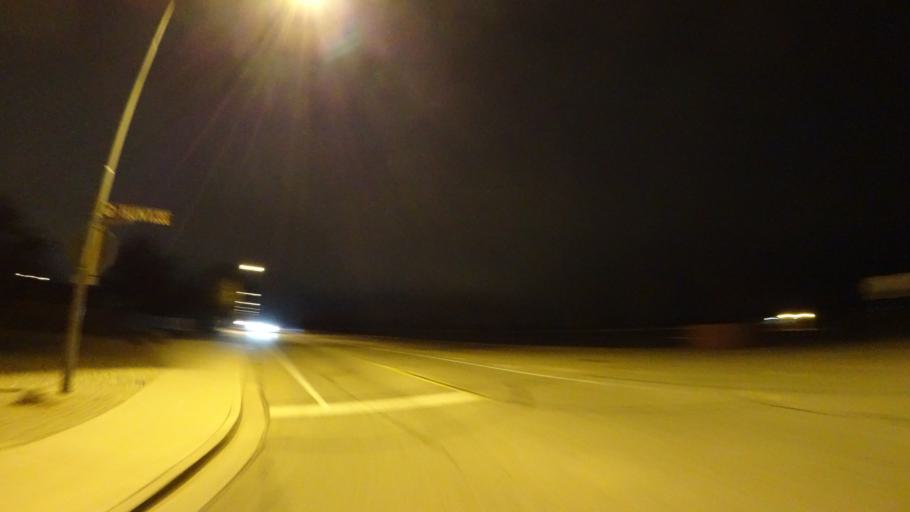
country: US
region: Arizona
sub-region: Maricopa County
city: Sun Lakes
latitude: 33.2048
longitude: -111.7554
